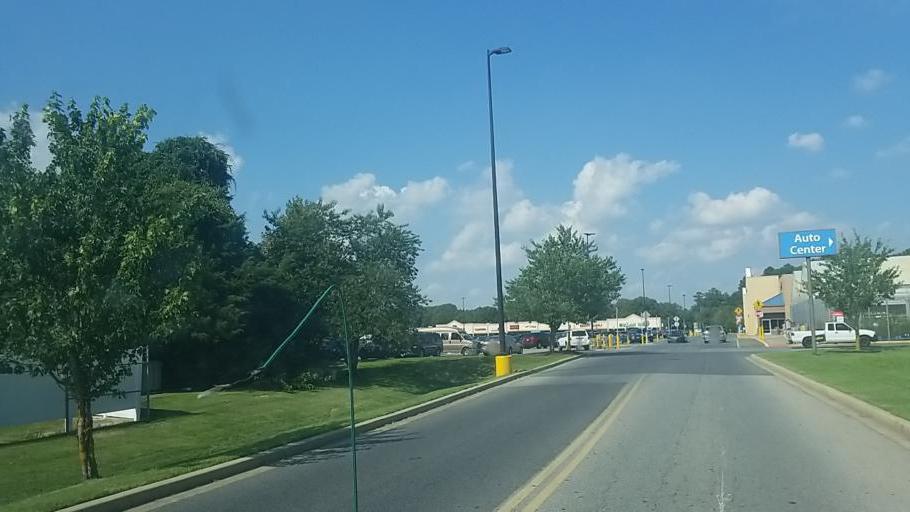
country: US
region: Maryland
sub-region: Wicomico County
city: Fruitland
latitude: 38.3278
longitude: -75.6121
